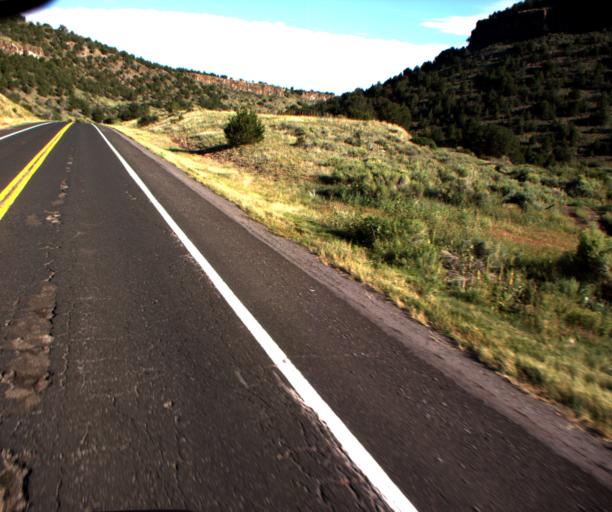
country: US
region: Arizona
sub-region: Apache County
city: Eagar
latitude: 34.0813
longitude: -109.2000
